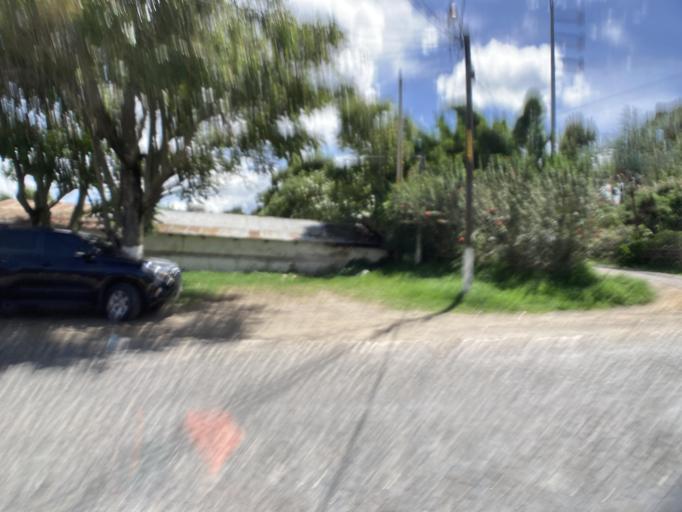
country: GT
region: Sacatepequez
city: Antigua Guatemala
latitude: 14.5460
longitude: -90.7332
